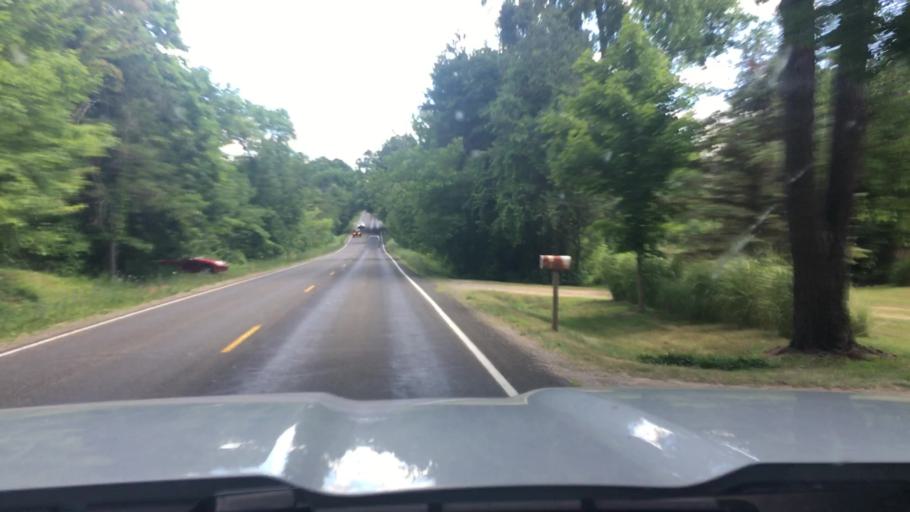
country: US
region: Michigan
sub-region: Kent County
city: Rockford
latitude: 43.1669
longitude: -85.6111
